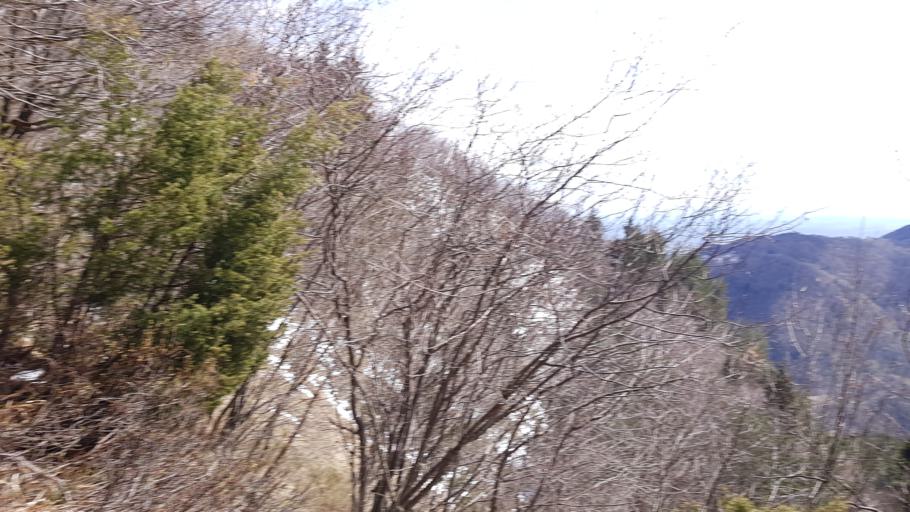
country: IT
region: Friuli Venezia Giulia
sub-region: Provincia di Udine
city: Trasaghis
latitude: 46.2732
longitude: 13.0195
